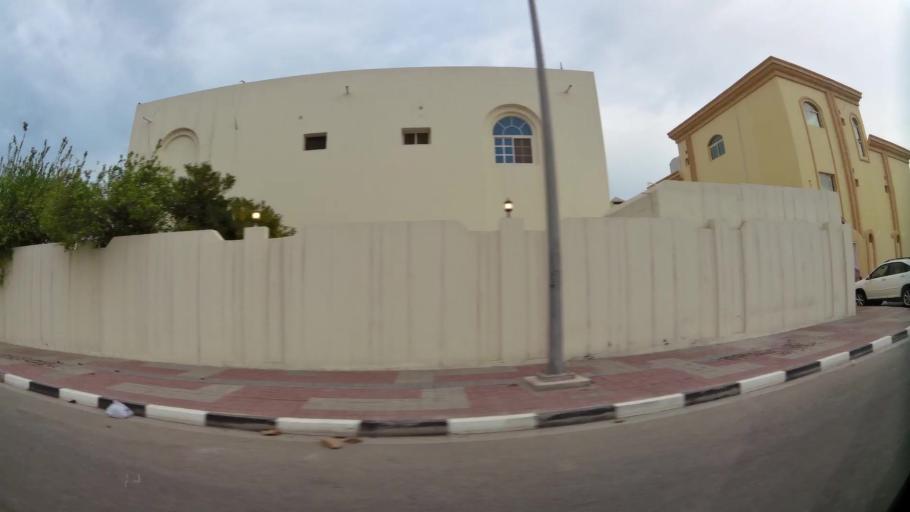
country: QA
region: Baladiyat ad Dawhah
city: Doha
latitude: 25.3386
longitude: 51.5092
